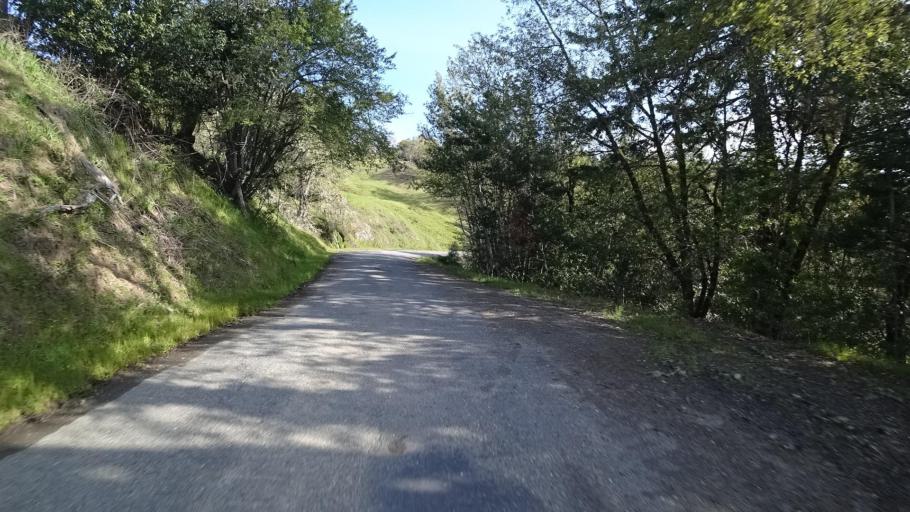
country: US
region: California
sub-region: Humboldt County
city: Hydesville
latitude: 40.6406
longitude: -123.8923
